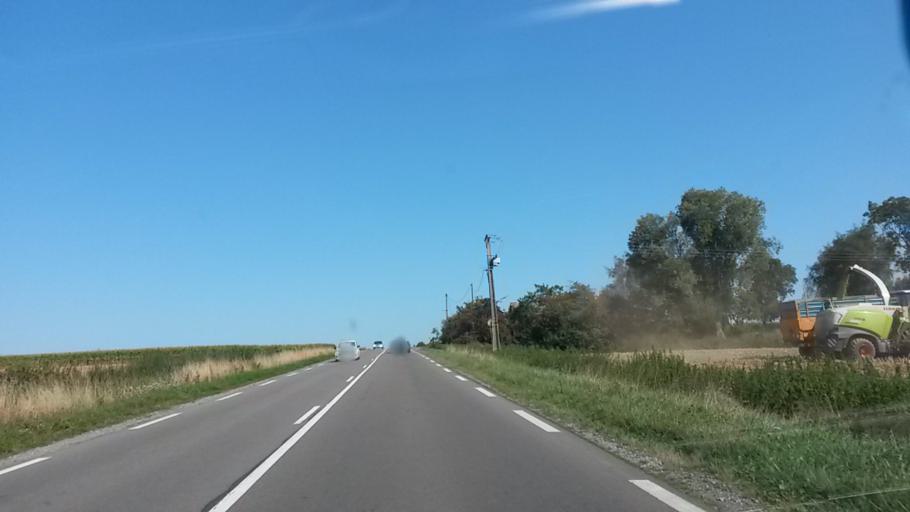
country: FR
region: Nord-Pas-de-Calais
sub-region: Departement du Nord
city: Avesnelles
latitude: 50.1854
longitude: 3.9521
